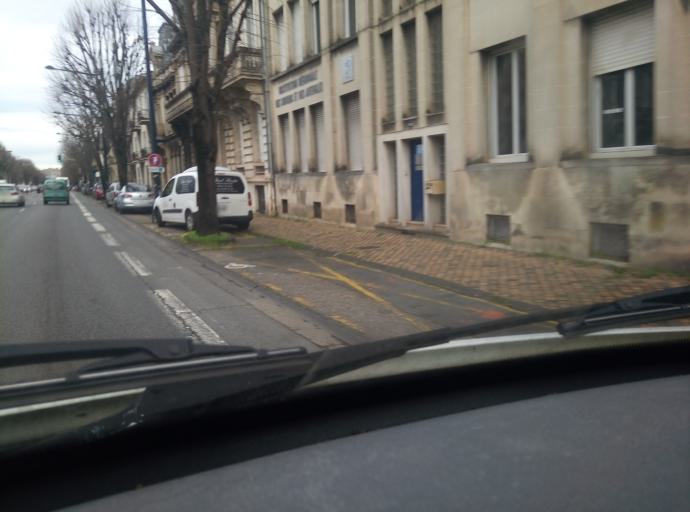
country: FR
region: Aquitaine
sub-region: Departement de la Gironde
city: Bordeaux
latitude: 44.8434
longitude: -0.5994
